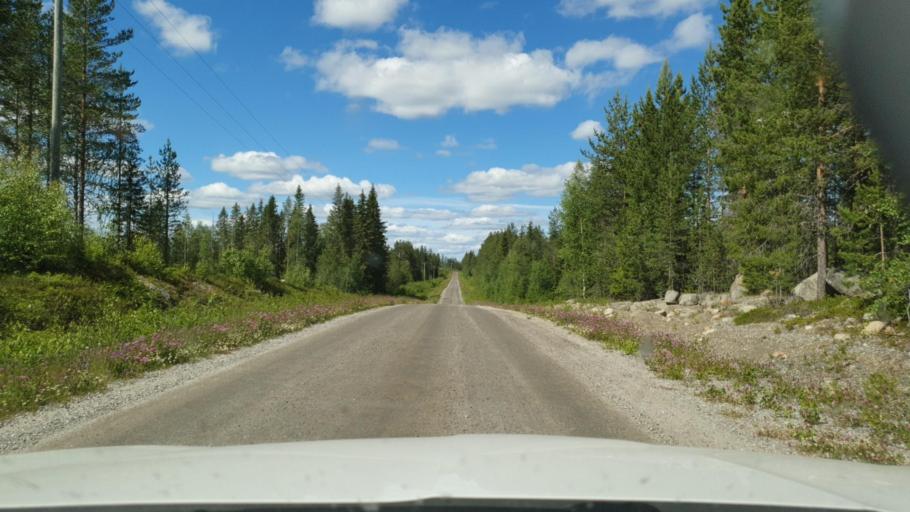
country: SE
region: Vaesterbotten
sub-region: Skelleftea Kommun
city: Backa
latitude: 65.1741
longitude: 21.0971
